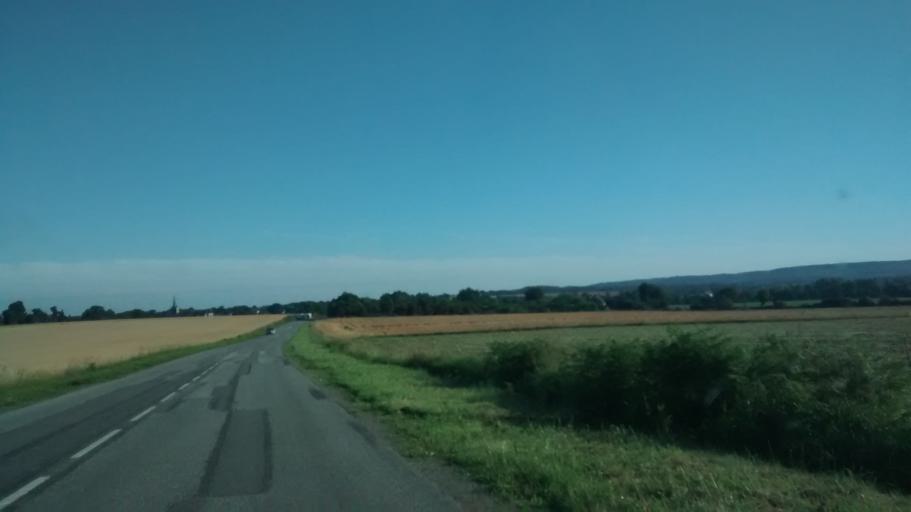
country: FR
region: Brittany
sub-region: Departement du Morbihan
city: Campeneac
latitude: 47.9482
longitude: -2.2876
